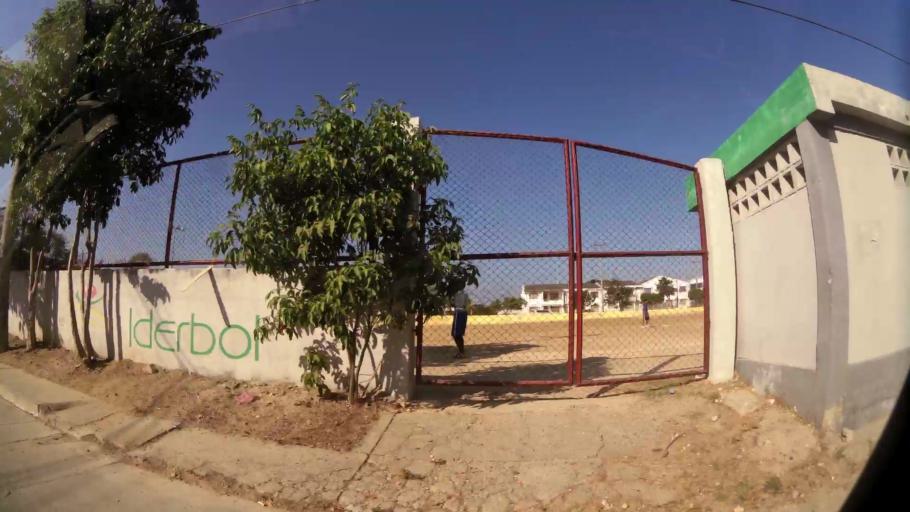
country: CO
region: Bolivar
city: Cartagena
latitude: 10.3916
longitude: -75.5051
